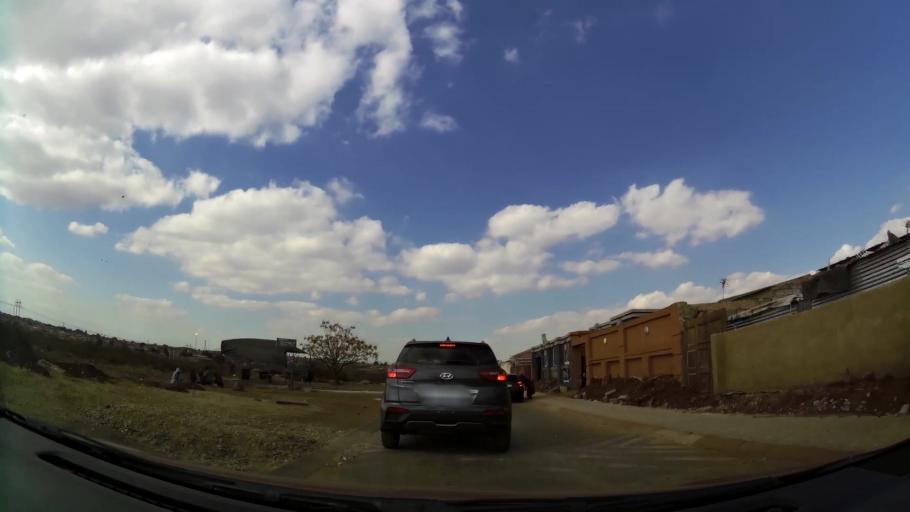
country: ZA
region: Gauteng
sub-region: Ekurhuleni Metropolitan Municipality
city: Tembisa
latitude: -25.9941
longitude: 28.2317
